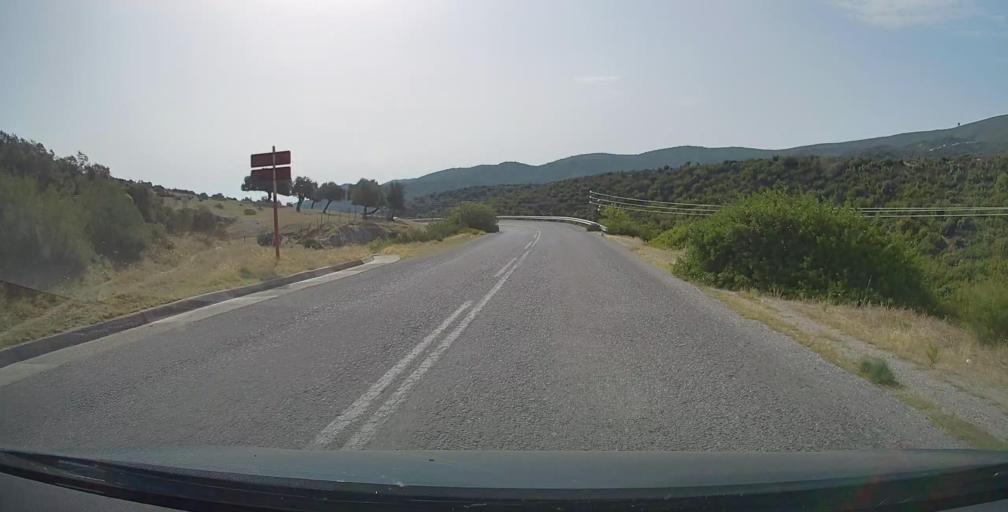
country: GR
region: Central Macedonia
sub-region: Nomos Chalkidikis
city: Sykia
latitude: 39.9918
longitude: 23.9646
